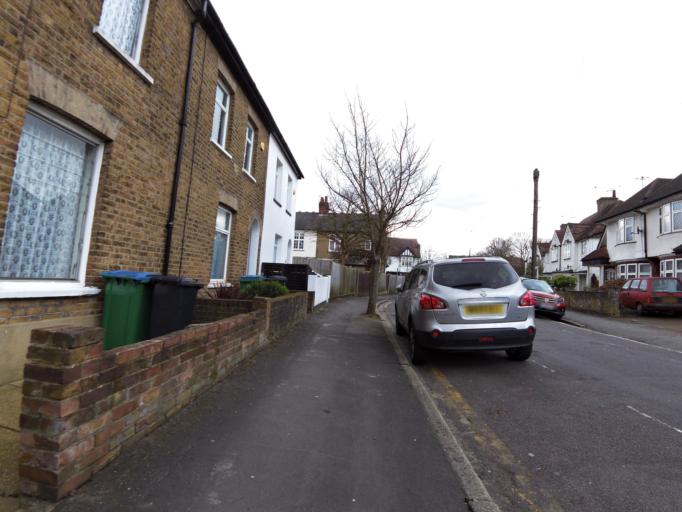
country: GB
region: England
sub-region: Hertfordshire
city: Watford
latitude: 51.6609
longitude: -0.3990
